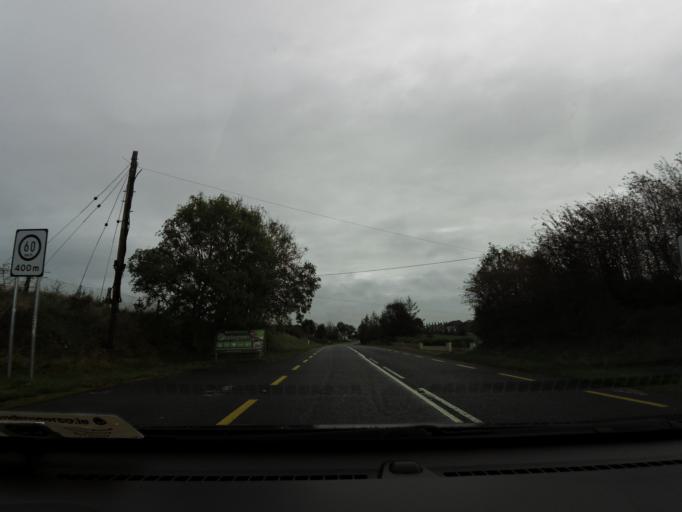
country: IE
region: Connaught
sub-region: County Galway
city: Tuam
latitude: 53.6113
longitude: -8.7541
